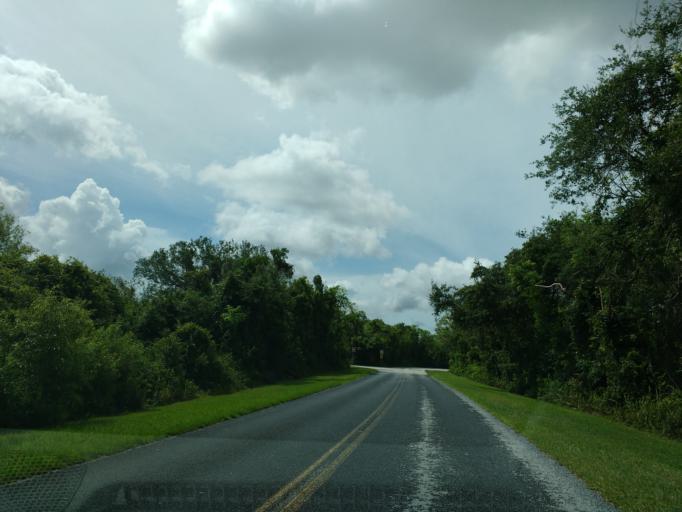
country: US
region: Florida
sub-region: Miami-Dade County
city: Florida City
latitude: 25.3844
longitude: -80.6108
